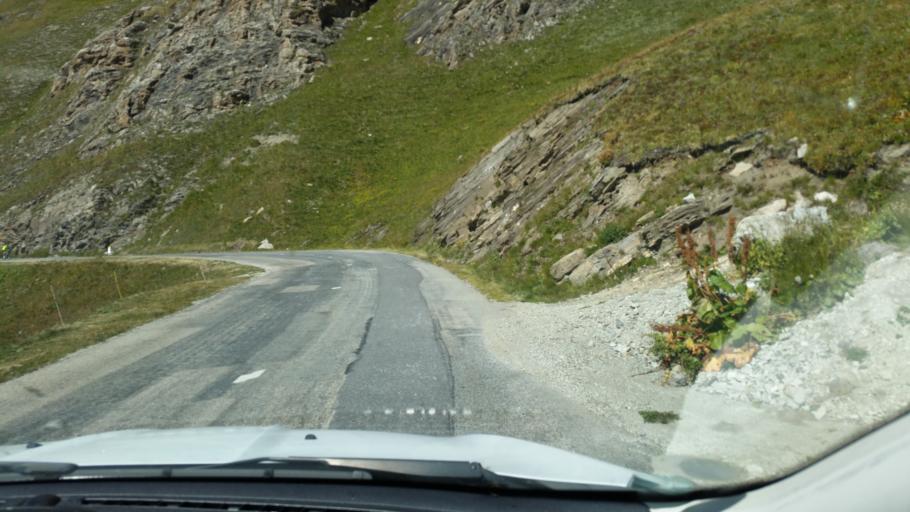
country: FR
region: Rhone-Alpes
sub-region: Departement de la Savoie
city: Val-d'Isere
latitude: 45.4000
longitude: 7.0426
